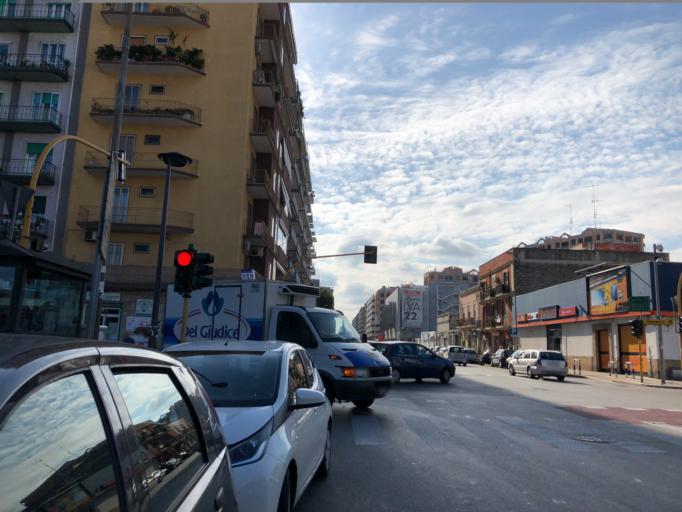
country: IT
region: Apulia
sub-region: Provincia di Bari
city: Bari
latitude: 41.1253
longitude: 16.8518
